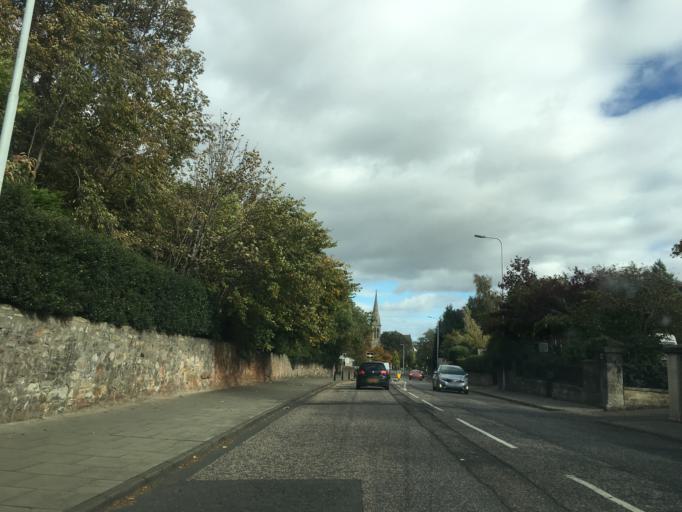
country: GB
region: Scotland
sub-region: Midlothian
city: Dalkeith
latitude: 55.8905
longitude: -3.0775
